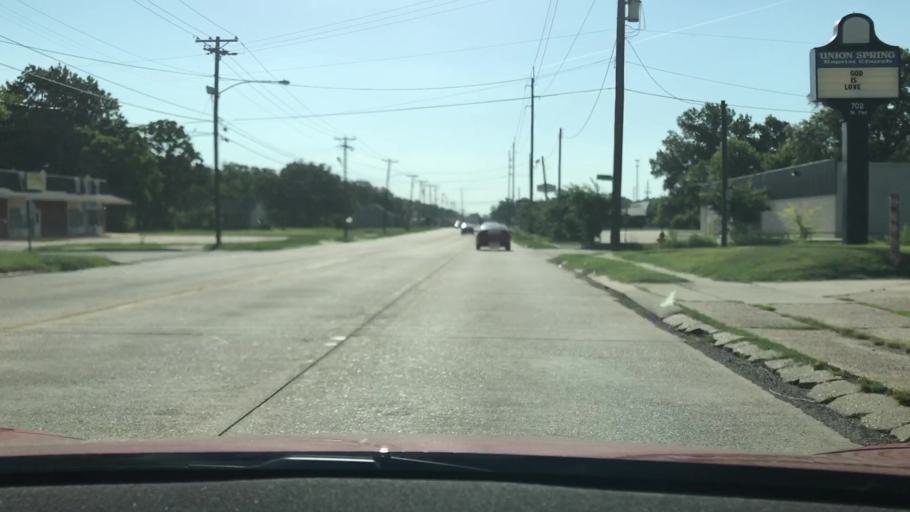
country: US
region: Louisiana
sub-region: Bossier Parish
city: Bossier City
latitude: 32.4420
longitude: -93.7699
